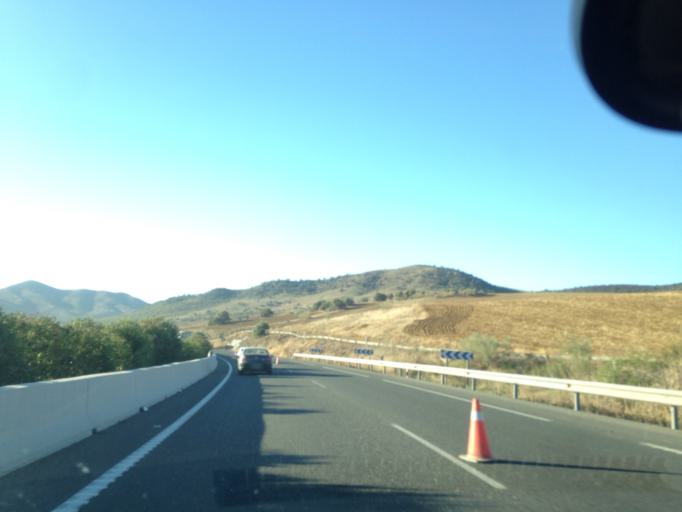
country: ES
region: Andalusia
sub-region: Provincia de Malaga
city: Casabermeja
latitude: 36.9327
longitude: -4.4455
